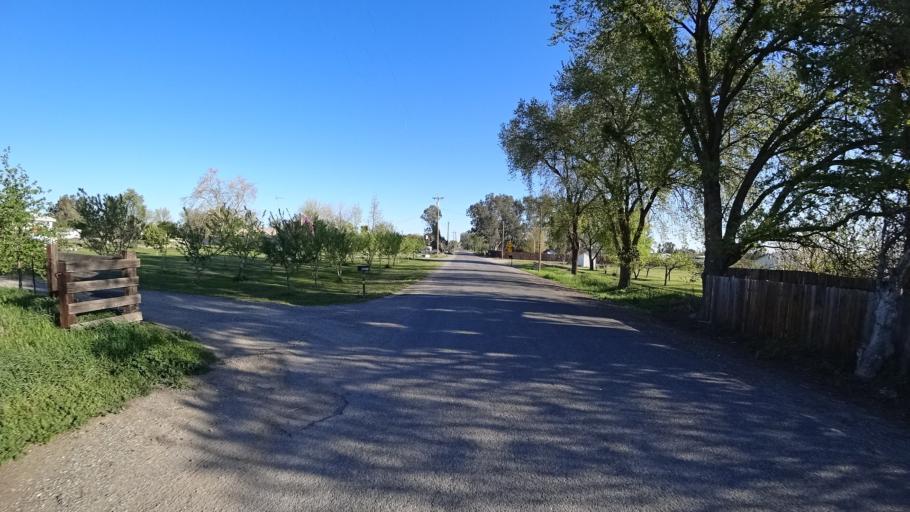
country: US
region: California
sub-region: Glenn County
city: Orland
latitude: 39.7652
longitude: -122.2297
